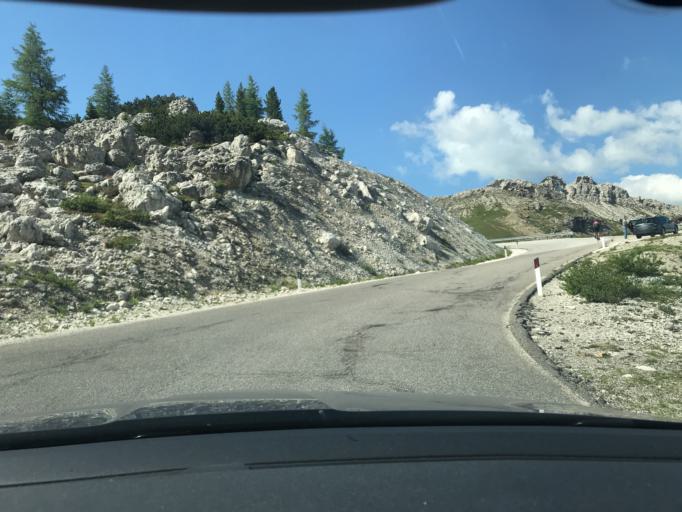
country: IT
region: Veneto
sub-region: Provincia di Belluno
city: Livinallongo del Col di Lana
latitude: 46.5340
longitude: 11.9897
